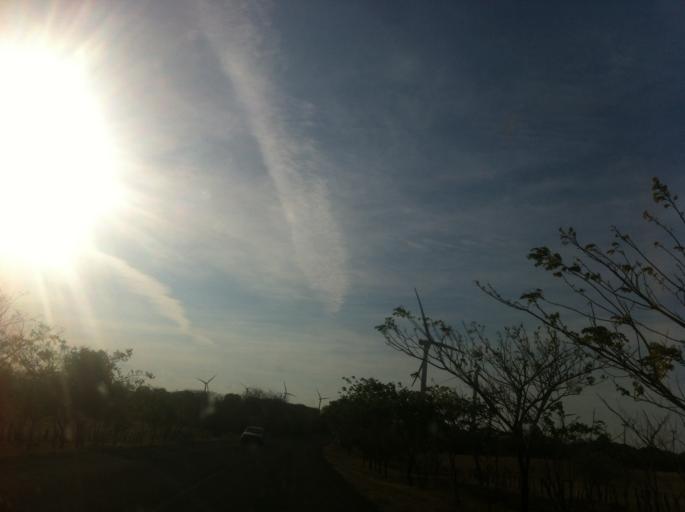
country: NI
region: Rivas
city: San Juan del Sur
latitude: 11.3062
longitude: -85.6920
